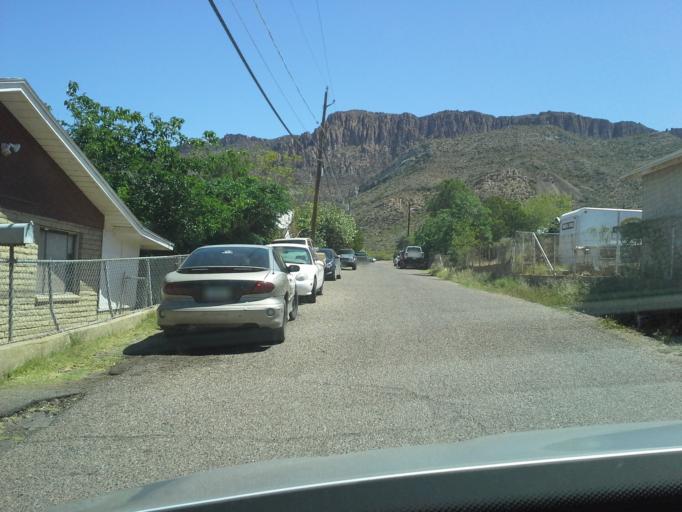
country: US
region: Arizona
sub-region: Pinal County
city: Superior
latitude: 33.2909
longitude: -111.1005
